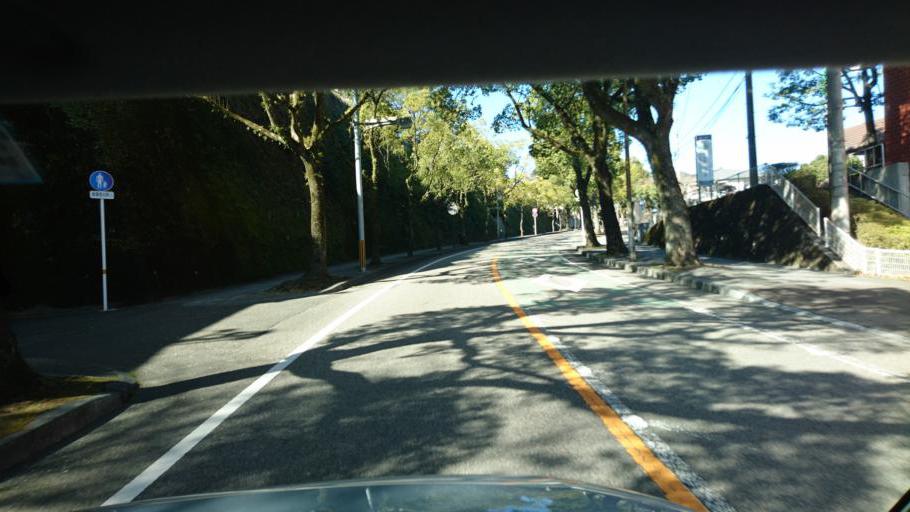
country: JP
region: Oita
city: Takedamachi
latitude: 32.7115
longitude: 131.3073
